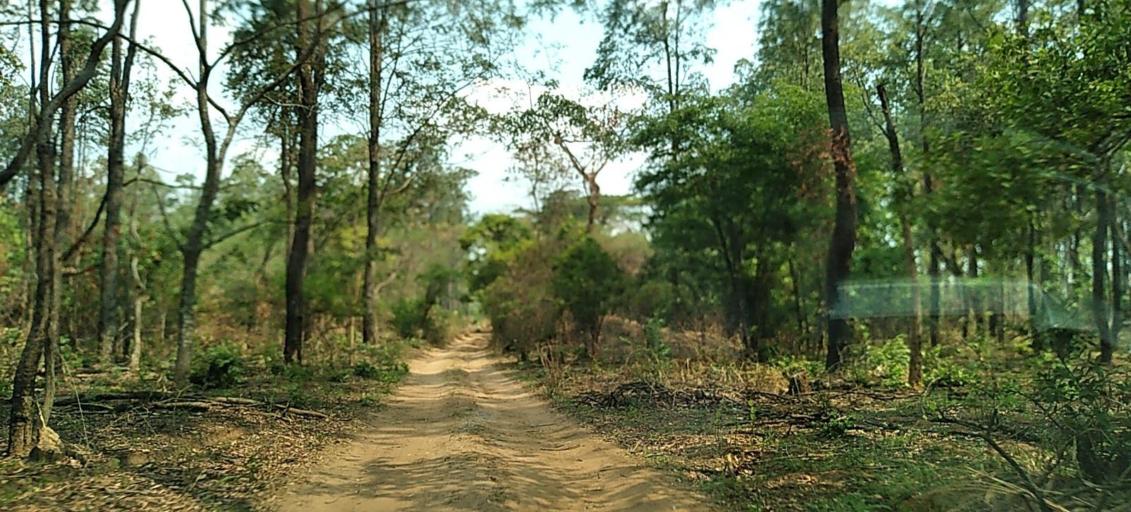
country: ZM
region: Copperbelt
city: Chingola
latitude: -12.7400
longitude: 27.7600
